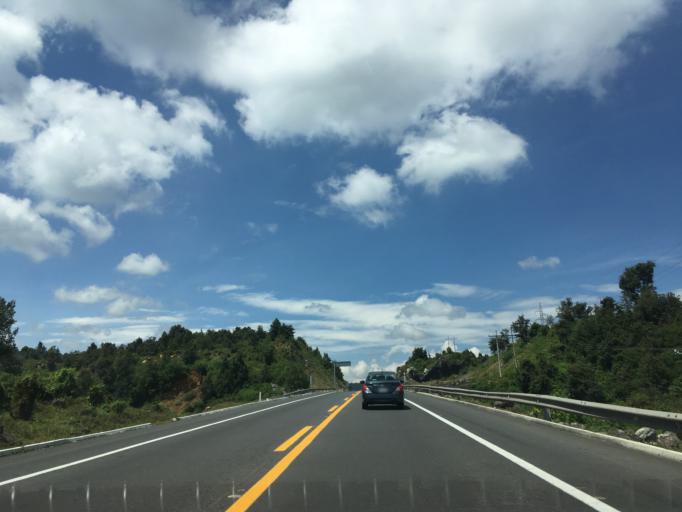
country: MX
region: Michoacan
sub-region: Patzcuaro
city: Colonia Vista Bella (Lomas del Peaje)
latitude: 19.4931
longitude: -101.6077
